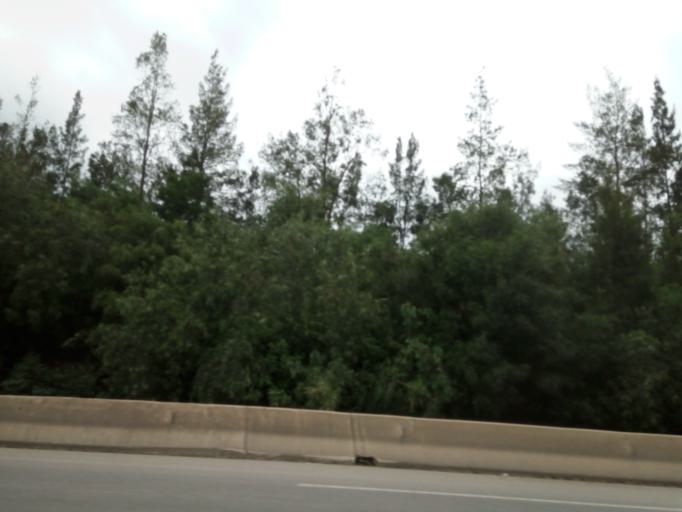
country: DZ
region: Blida
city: Chiffa
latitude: 36.4671
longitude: 2.7641
